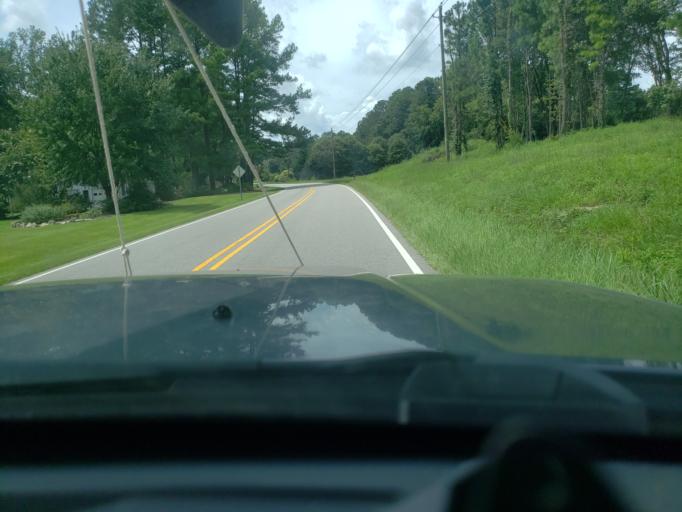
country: US
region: North Carolina
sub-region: Wake County
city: Zebulon
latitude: 35.8822
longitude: -78.3797
